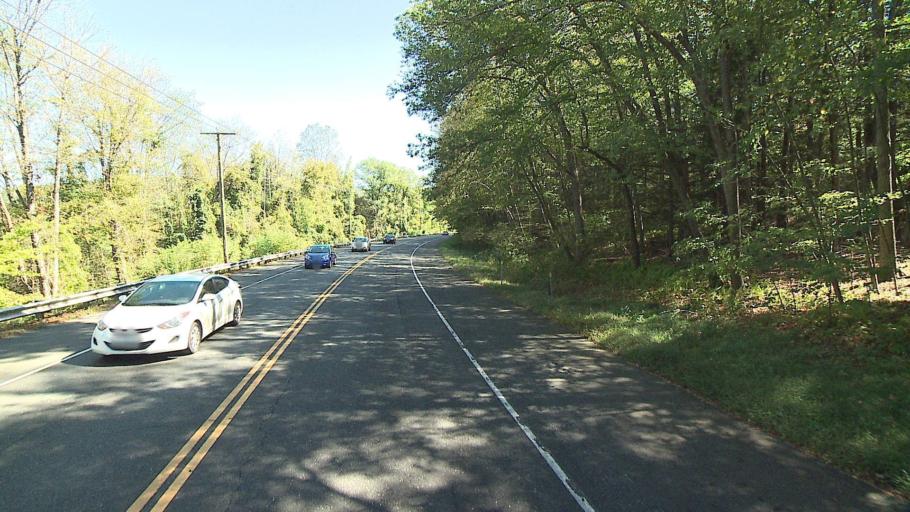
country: US
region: Connecticut
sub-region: Hartford County
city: Collinsville
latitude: 41.8335
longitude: -72.9355
